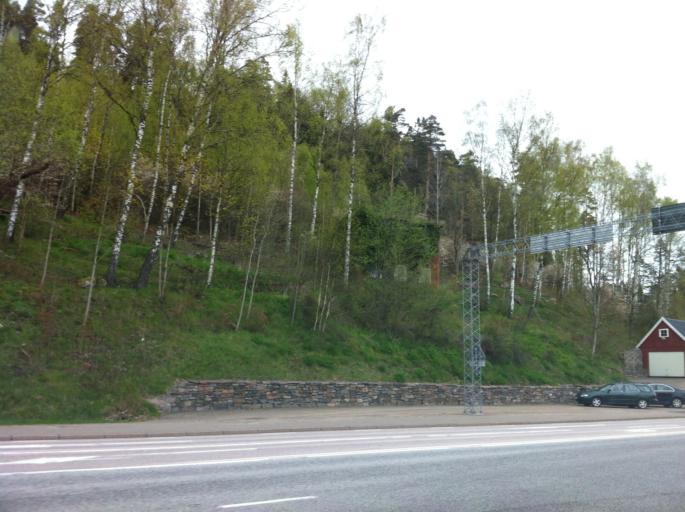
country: SE
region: Halland
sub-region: Falkenbergs Kommun
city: Falkenberg
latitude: 57.1374
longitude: 12.7108
